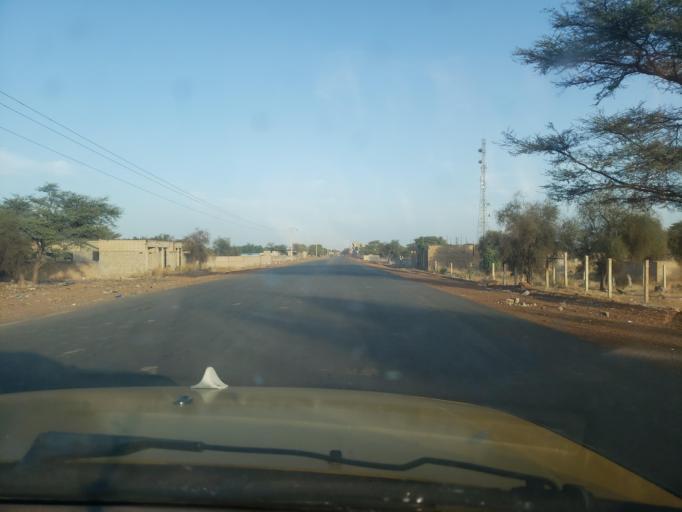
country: SN
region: Louga
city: Dara
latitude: 15.3499
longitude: -15.4946
